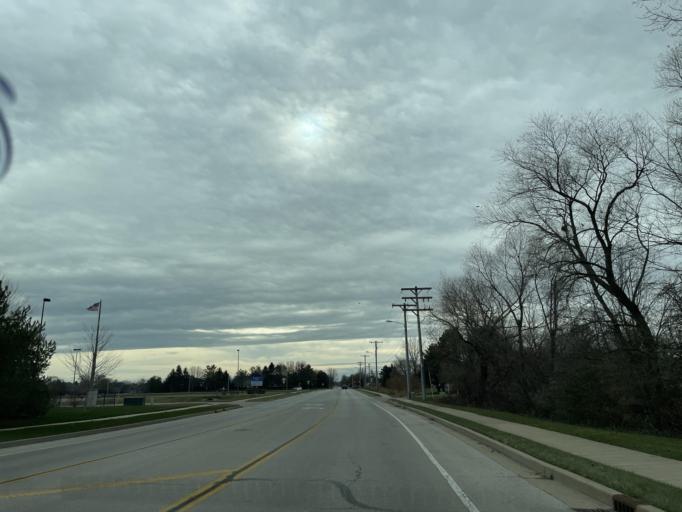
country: US
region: Illinois
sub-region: Sangamon County
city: Jerome
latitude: 39.7733
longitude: -89.7299
